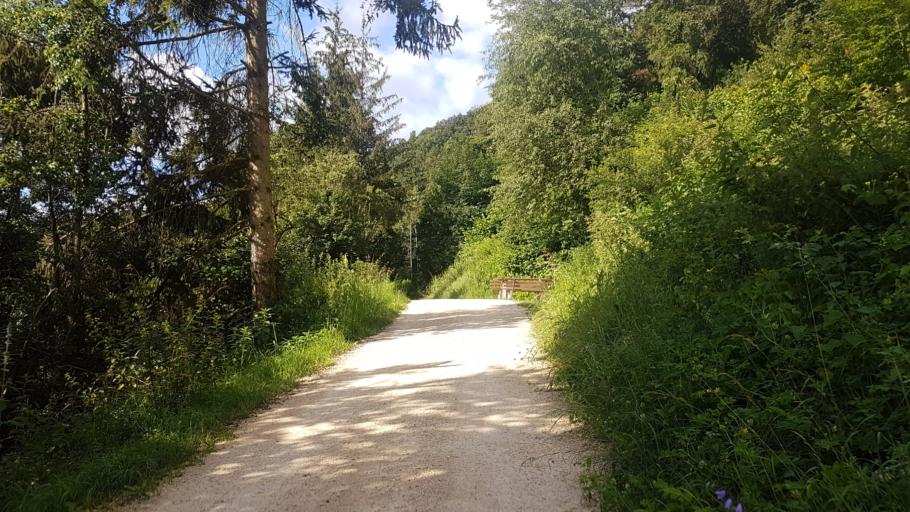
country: DE
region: Bavaria
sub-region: Upper Bavaria
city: Walting
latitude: 48.9465
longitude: 11.3528
